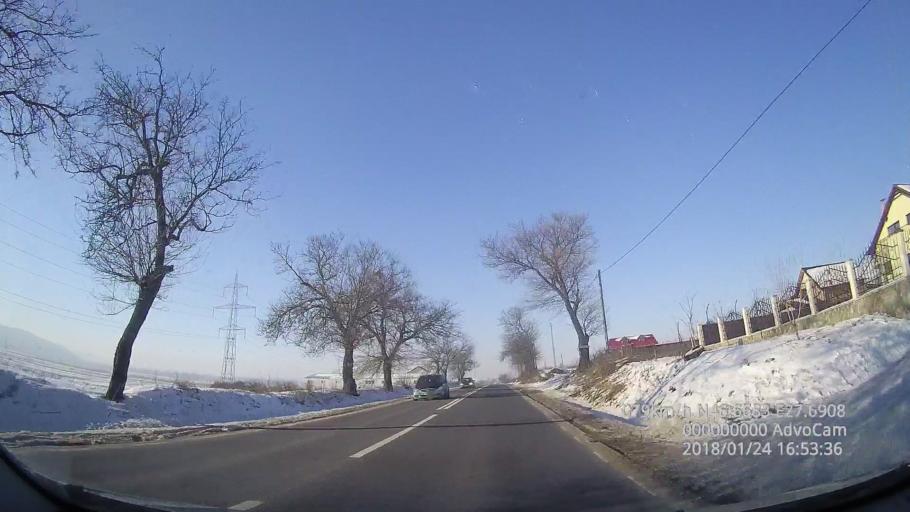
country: RO
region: Vaslui
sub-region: Municipiul Vaslui
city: Brodoc
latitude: 46.6687
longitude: 27.6904
